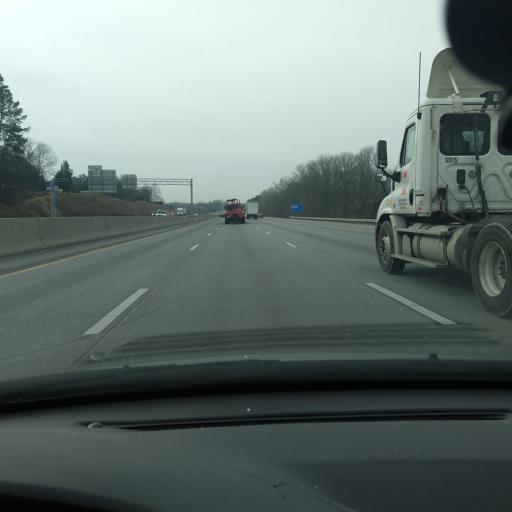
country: US
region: North Carolina
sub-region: Cabarrus County
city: Kannapolis
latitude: 35.4264
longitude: -80.6683
